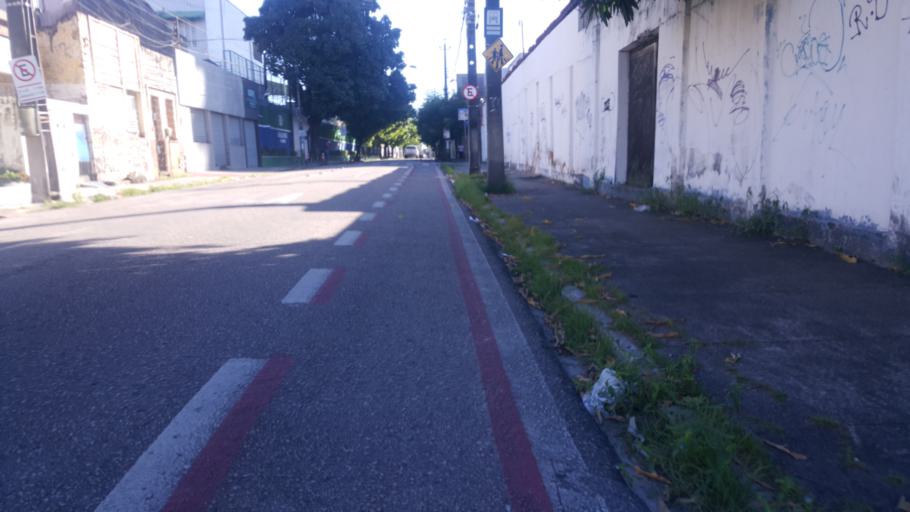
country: BR
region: Ceara
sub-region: Fortaleza
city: Fortaleza
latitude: -3.7420
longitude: -38.5333
